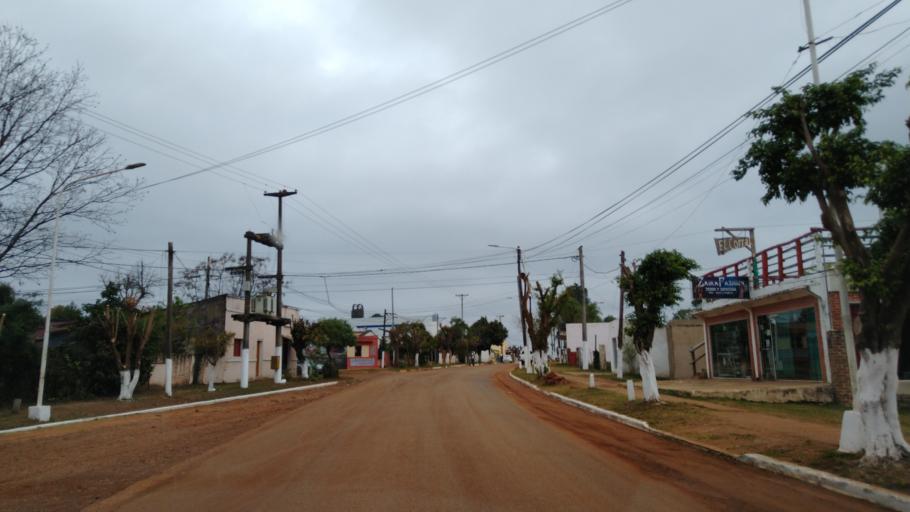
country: AR
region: Corrientes
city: Alvear
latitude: -29.0892
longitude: -56.5469
